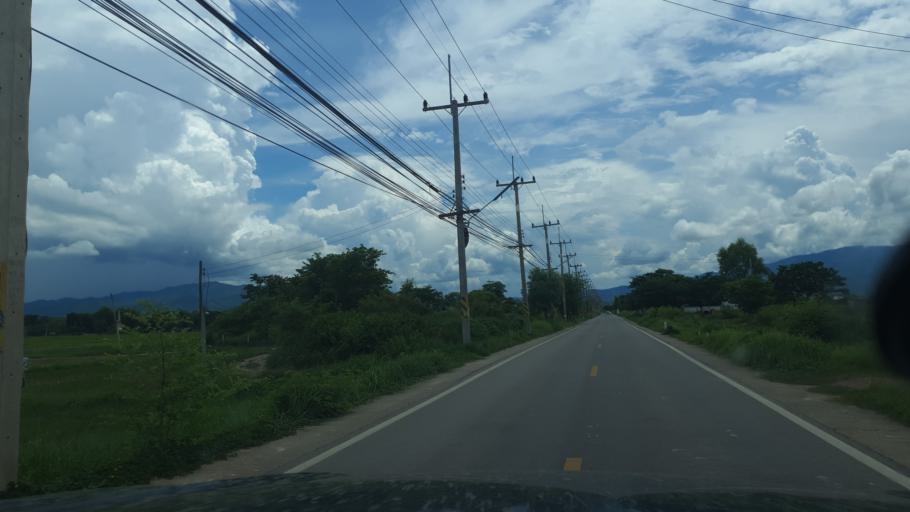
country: TH
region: Lampang
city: Sop Prap
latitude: 17.8832
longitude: 99.3783
